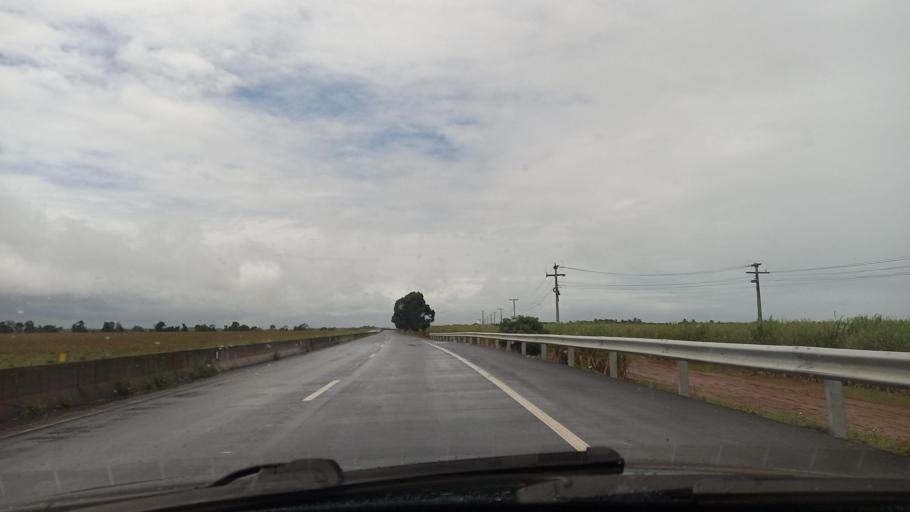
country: BR
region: Alagoas
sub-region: Campo Alegre
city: Campo Alegre
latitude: -9.8008
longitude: -36.2856
